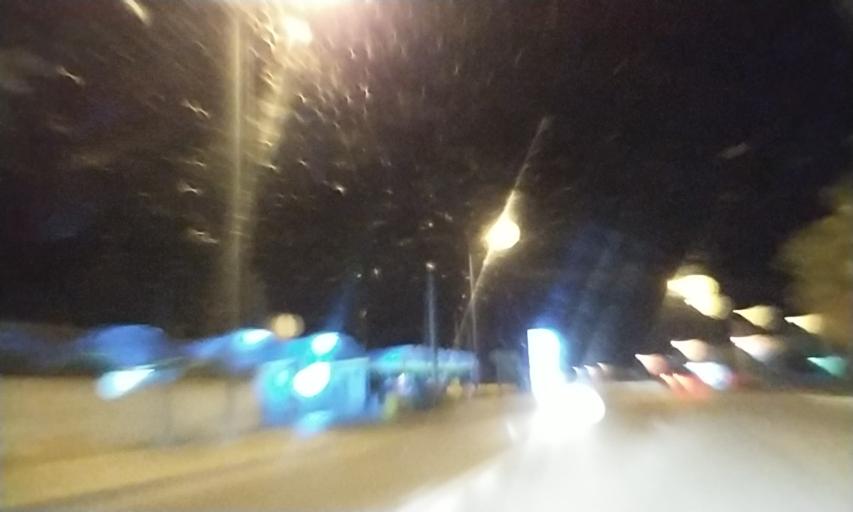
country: PT
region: Castelo Branco
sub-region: Concelho do Fundao
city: Fundao
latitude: 40.1520
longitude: -7.4974
